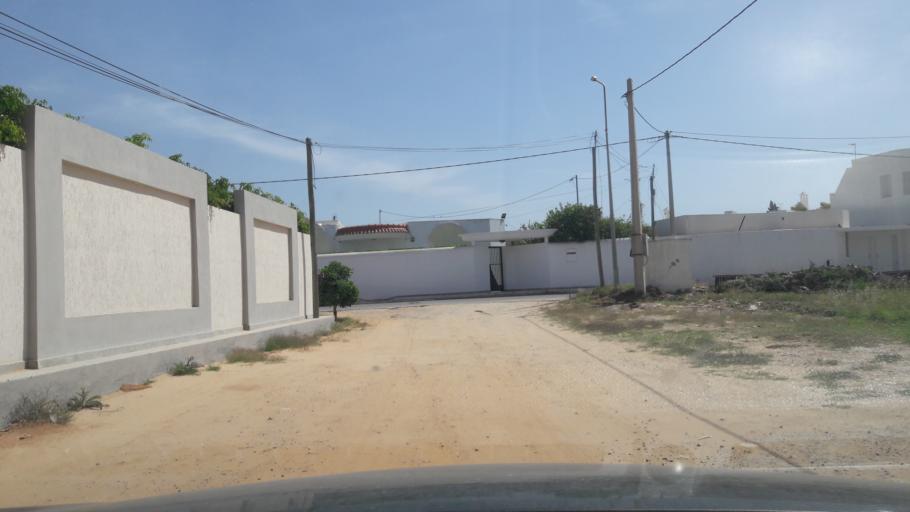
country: TN
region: Safaqis
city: Al Qarmadah
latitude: 34.7907
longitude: 10.7558
